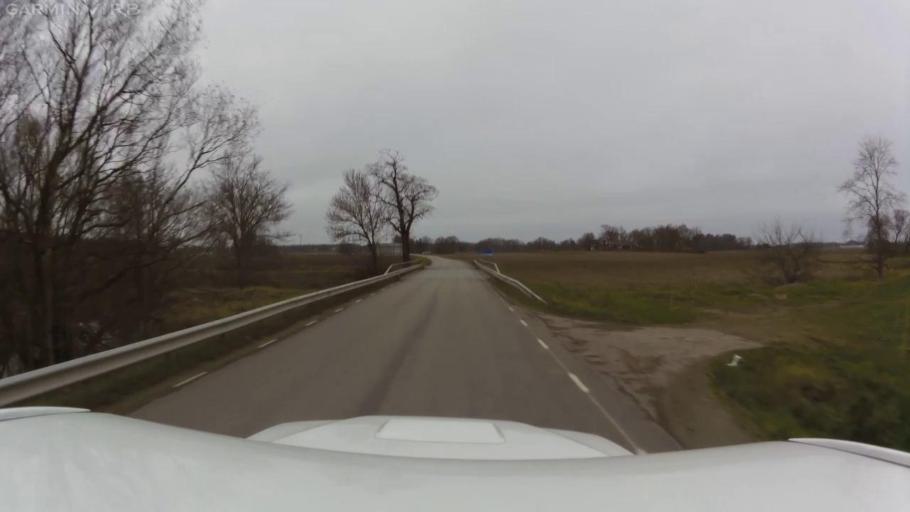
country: SE
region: OEstergoetland
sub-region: Linkopings Kommun
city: Vikingstad
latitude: 58.3743
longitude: 15.4350
